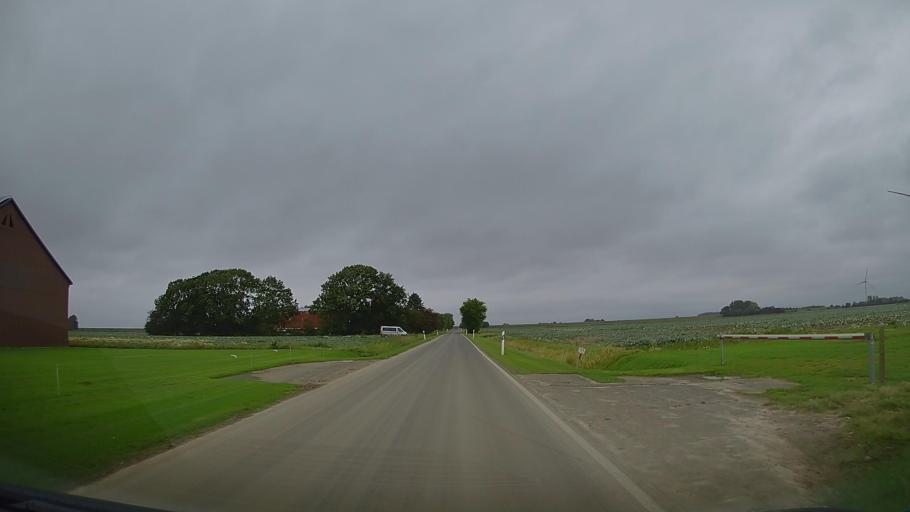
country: DE
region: Schleswig-Holstein
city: Friedrichskoog
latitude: 54.0172
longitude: 8.9078
